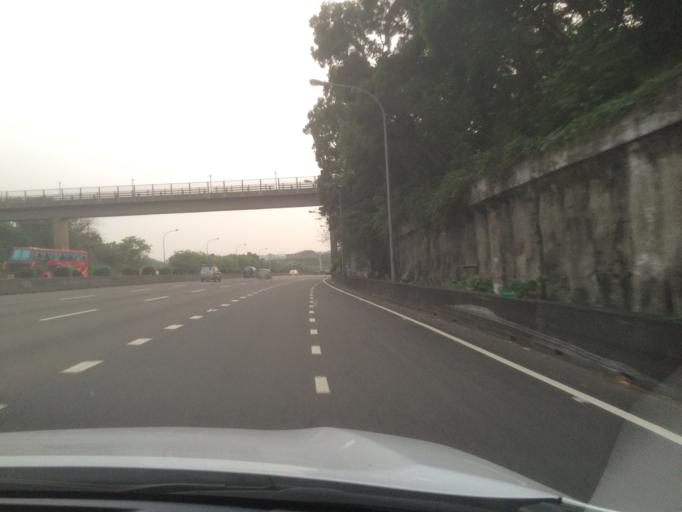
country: TW
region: Taiwan
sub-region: Hsinchu
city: Hsinchu
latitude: 24.7517
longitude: 120.9829
